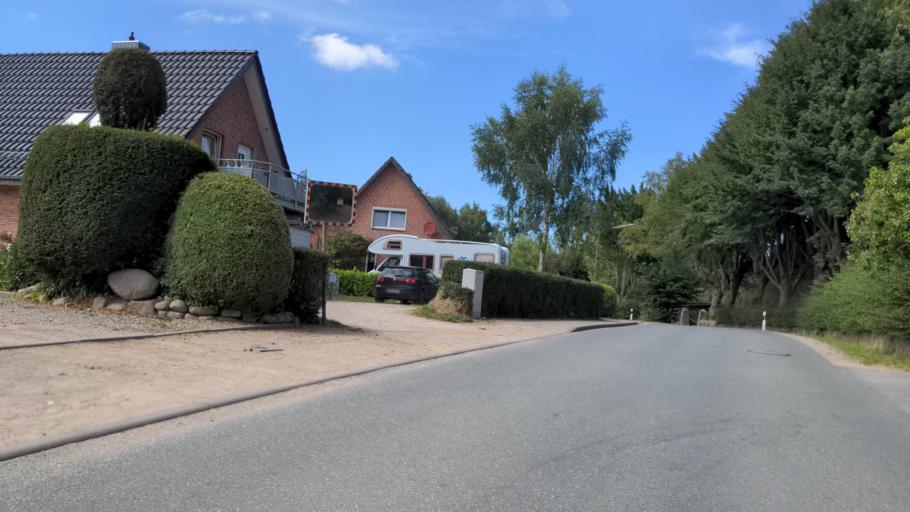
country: DE
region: Schleswig-Holstein
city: Malente
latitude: 54.1811
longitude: 10.5404
